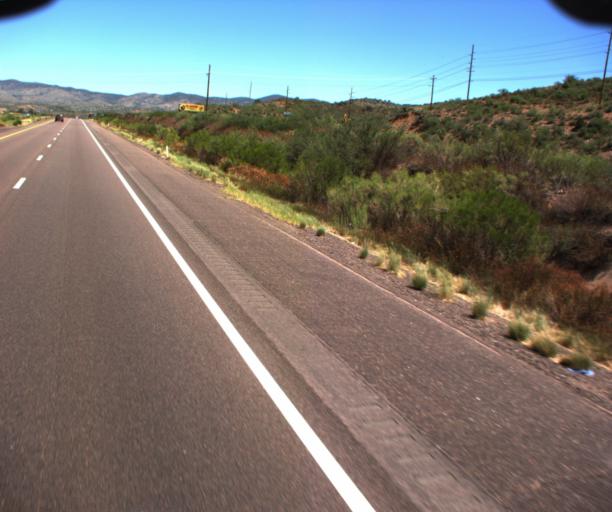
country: US
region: Arizona
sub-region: Gila County
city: Payson
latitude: 34.0924
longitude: -111.3534
